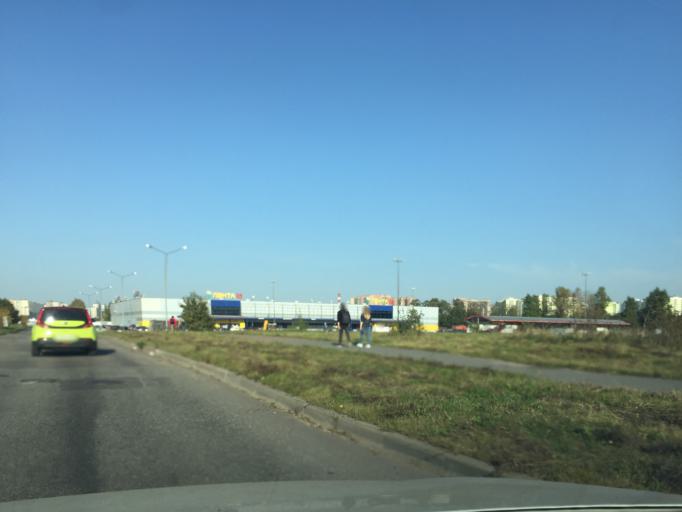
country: RU
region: Leningrad
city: Murino
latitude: 60.0291
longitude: 30.4332
